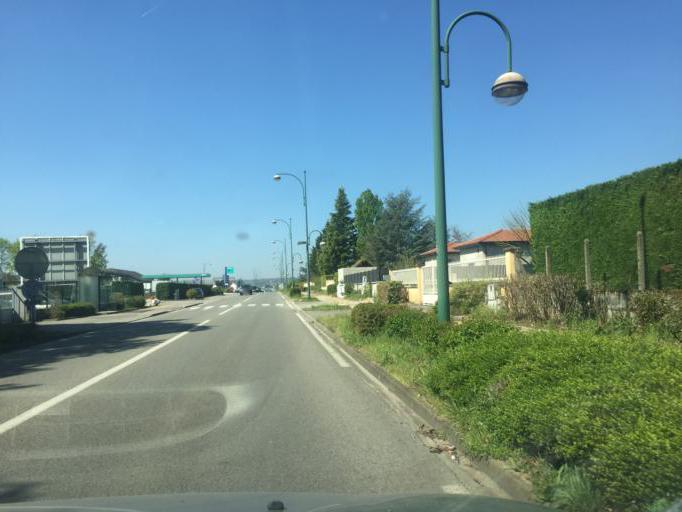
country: FR
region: Rhone-Alpes
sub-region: Departement de l'Ain
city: Balan
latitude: 45.8494
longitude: 5.1079
